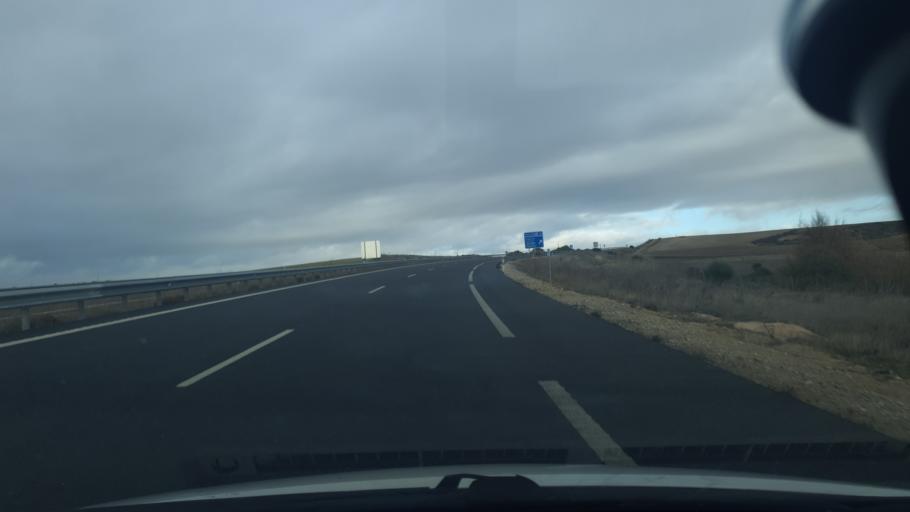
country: ES
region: Castille and Leon
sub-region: Provincia de Segovia
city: Cuellar
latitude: 41.3971
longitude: -4.2928
